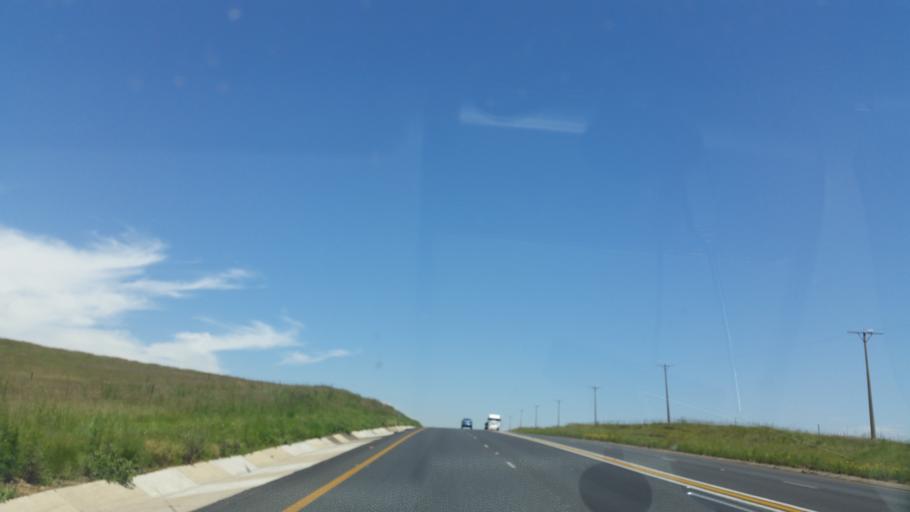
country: ZA
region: Orange Free State
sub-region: Thabo Mofutsanyana District Municipality
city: Harrismith
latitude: -28.3665
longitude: 29.3489
